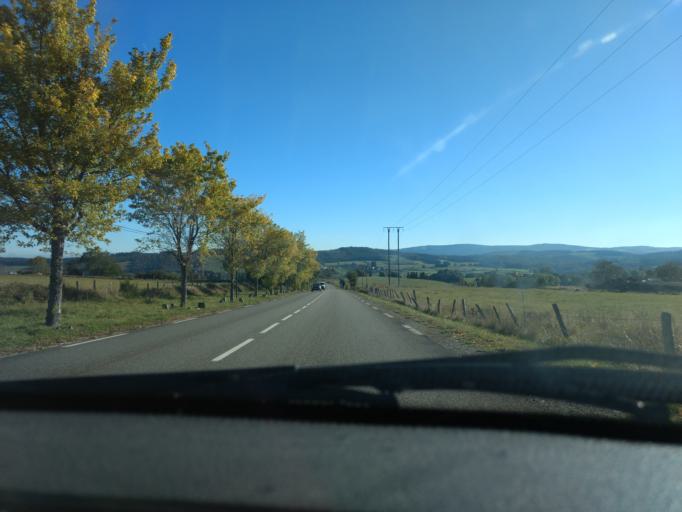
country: FR
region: Midi-Pyrenees
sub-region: Departement de l'Aveyron
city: Laguiole
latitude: 44.7728
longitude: 2.8890
